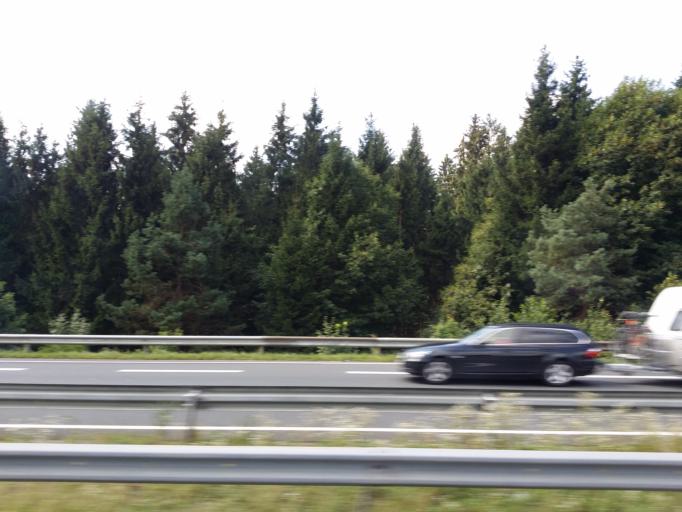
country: SI
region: Kranj
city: Mlaka pri Kranju
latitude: 46.2661
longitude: 14.3393
